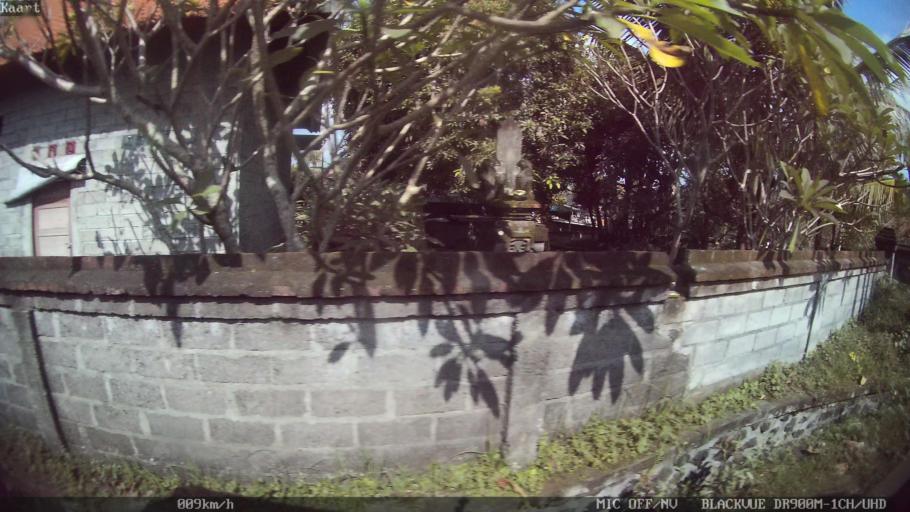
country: ID
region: Bali
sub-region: Kabupaten Gianyar
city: Ubud
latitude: -8.5113
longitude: 115.2858
